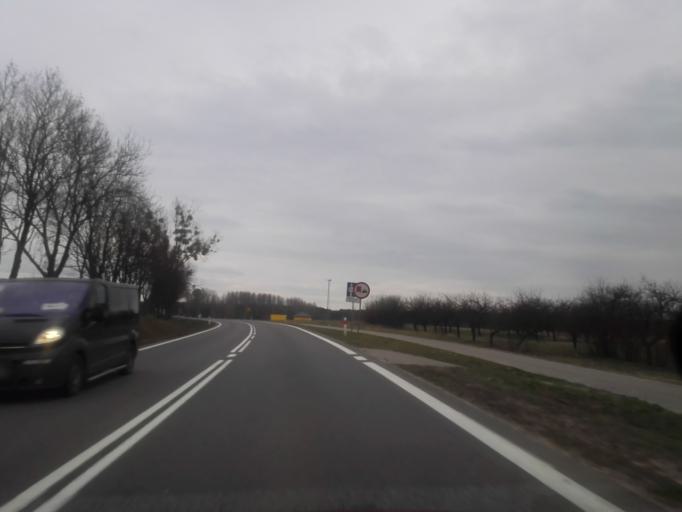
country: PL
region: Podlasie
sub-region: Powiat grajewski
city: Rajgrod
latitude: 53.7232
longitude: 22.6768
